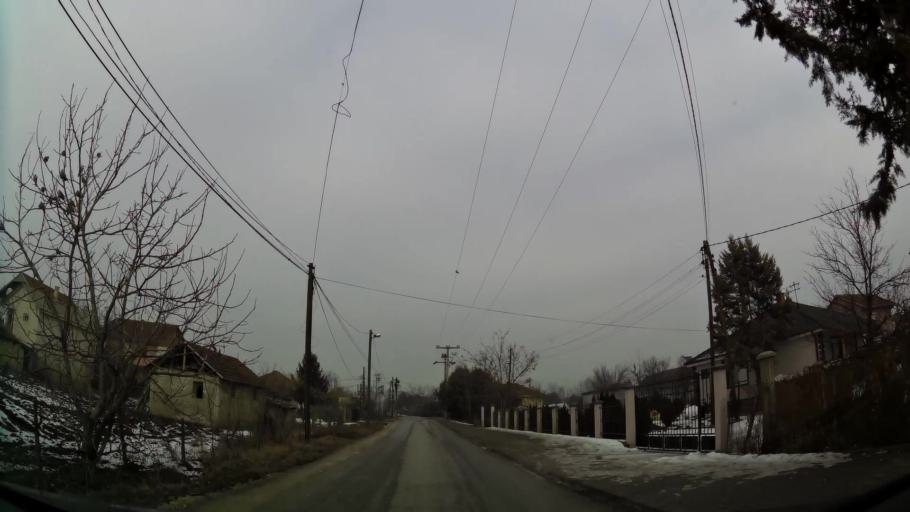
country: MK
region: Ilinden
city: Ilinden
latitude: 41.9953
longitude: 21.5816
